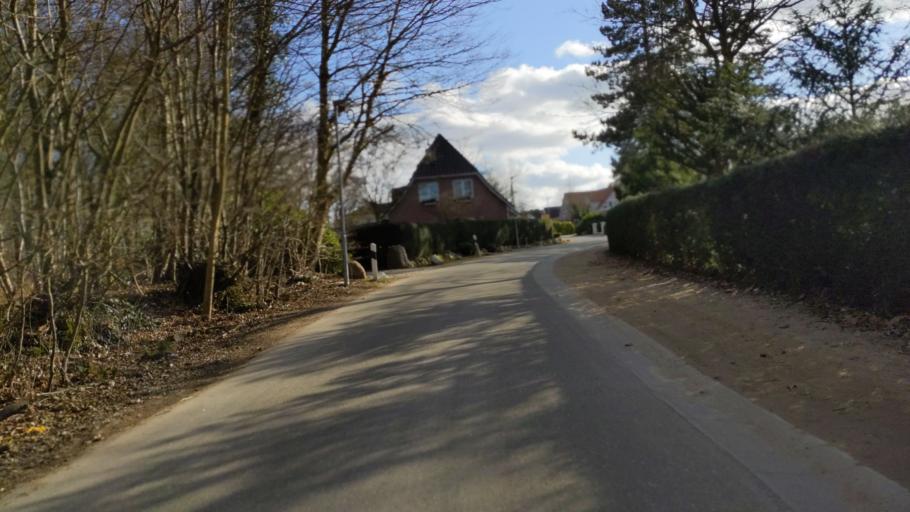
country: DE
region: Schleswig-Holstein
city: Timmendorfer Strand
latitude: 54.0032
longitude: 10.7548
